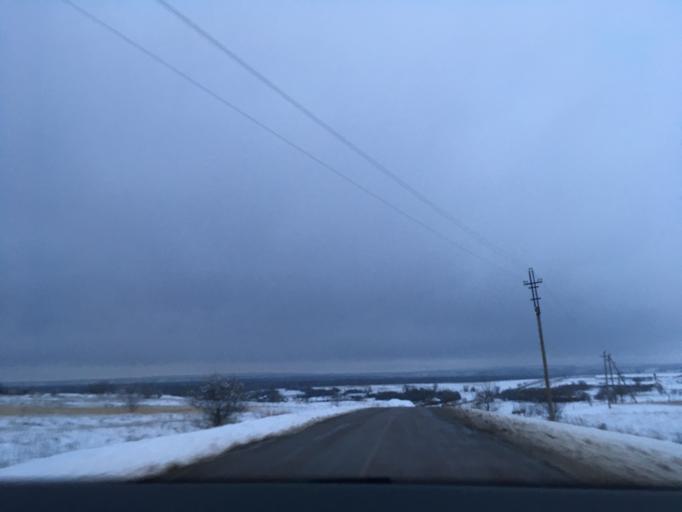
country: RU
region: Voronezj
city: Verkhniy Mamon
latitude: 50.0714
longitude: 40.3121
